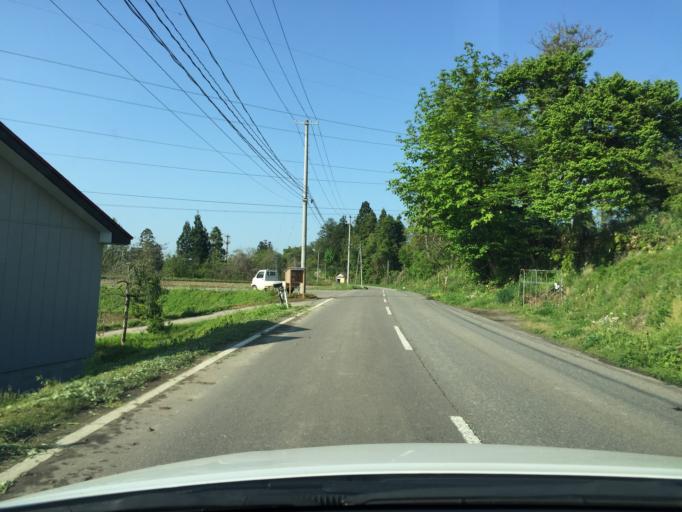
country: JP
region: Fukushima
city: Kitakata
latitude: 37.6638
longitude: 139.7773
